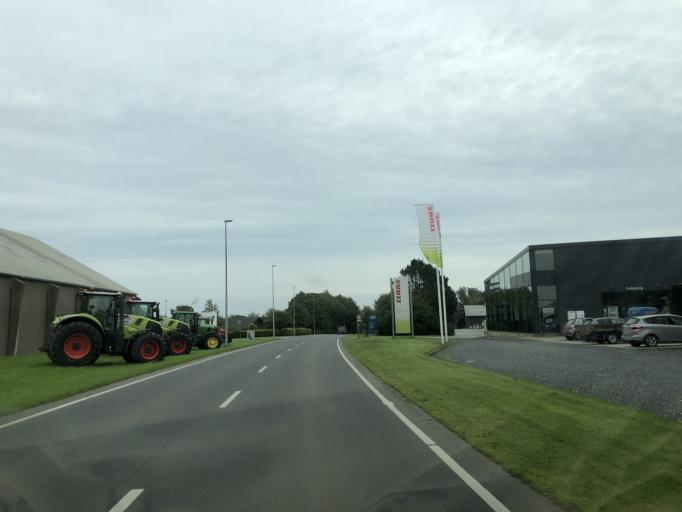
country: DK
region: North Denmark
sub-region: Morso Kommune
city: Nykobing Mors
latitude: 56.7996
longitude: 8.8433
